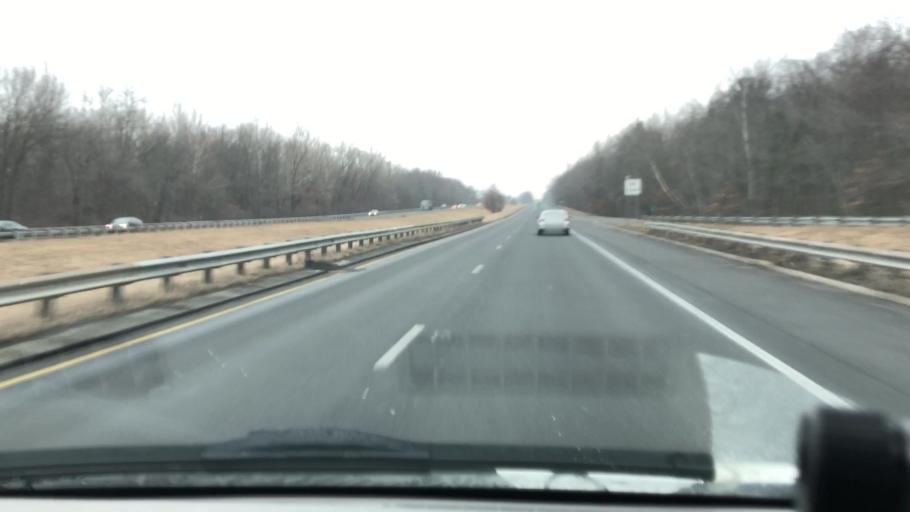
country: US
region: Massachusetts
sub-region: Hampshire County
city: Hatfield
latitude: 42.3962
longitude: -72.6291
